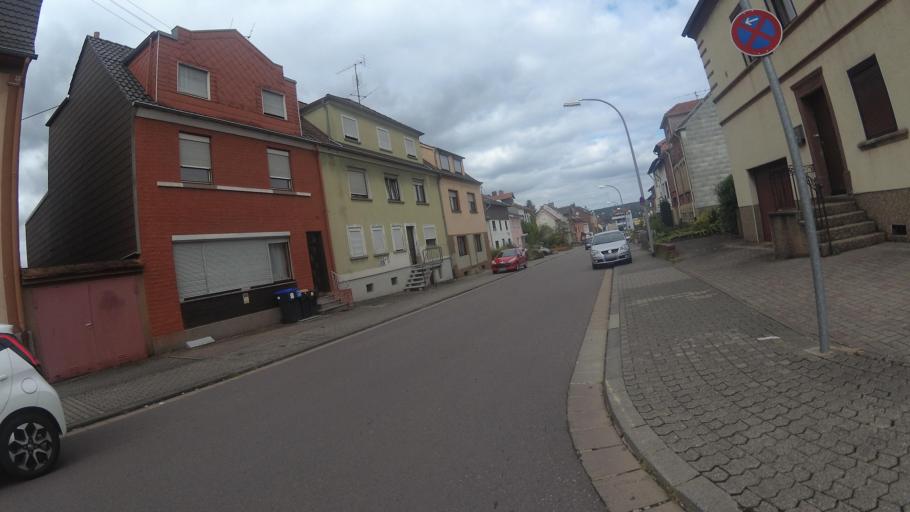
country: FR
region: Lorraine
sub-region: Departement de la Moselle
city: Schoeneck
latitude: 49.2376
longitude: 6.9152
